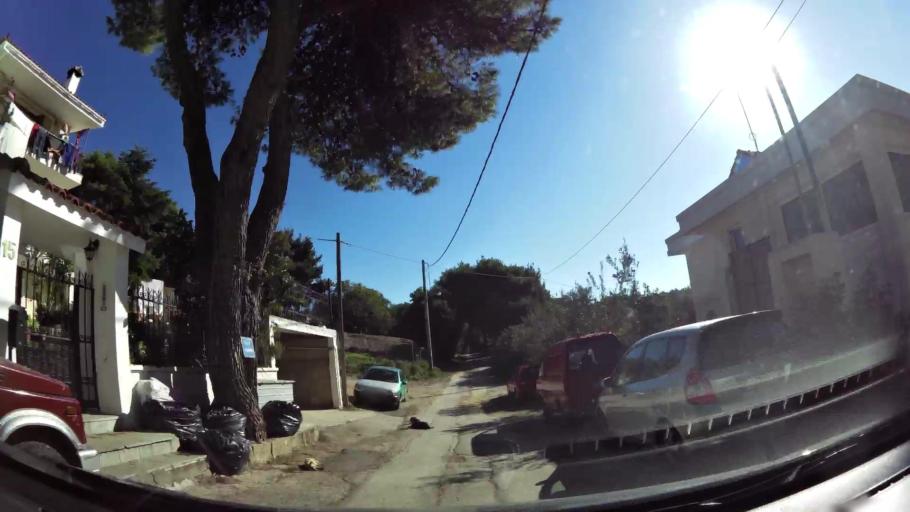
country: GR
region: Attica
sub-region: Nomarchia Anatolikis Attikis
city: Anoixi
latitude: 38.1323
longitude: 23.8672
